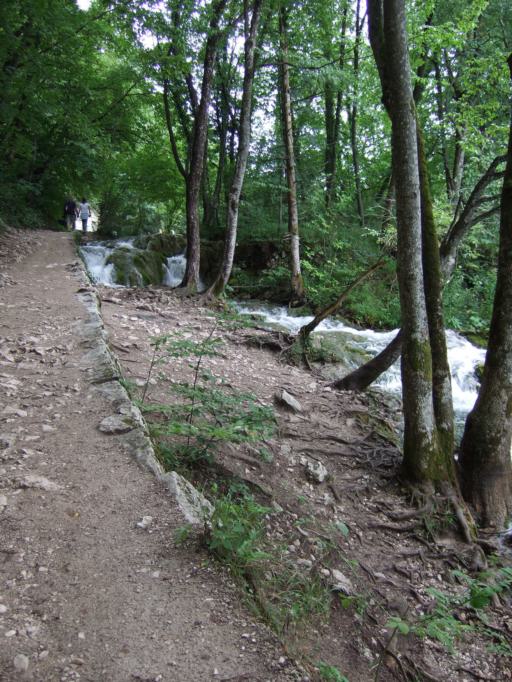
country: HR
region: Licko-Senjska
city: Jezerce
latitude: 44.8947
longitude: 15.6097
